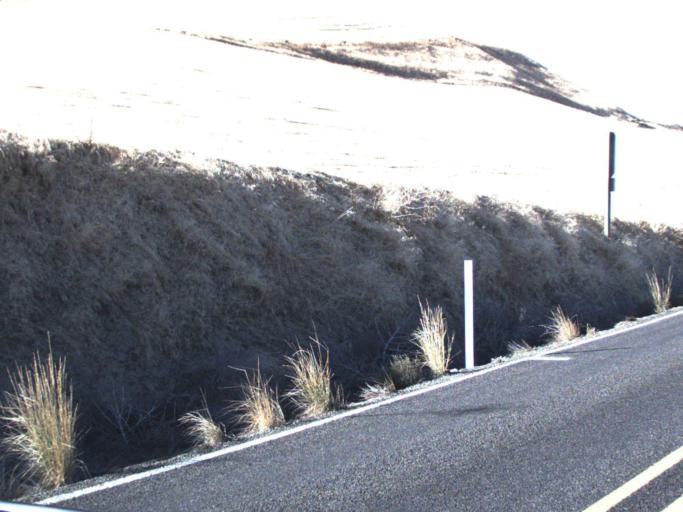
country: US
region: Washington
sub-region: Walla Walla County
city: Walla Walla
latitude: 46.1889
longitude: -118.3835
